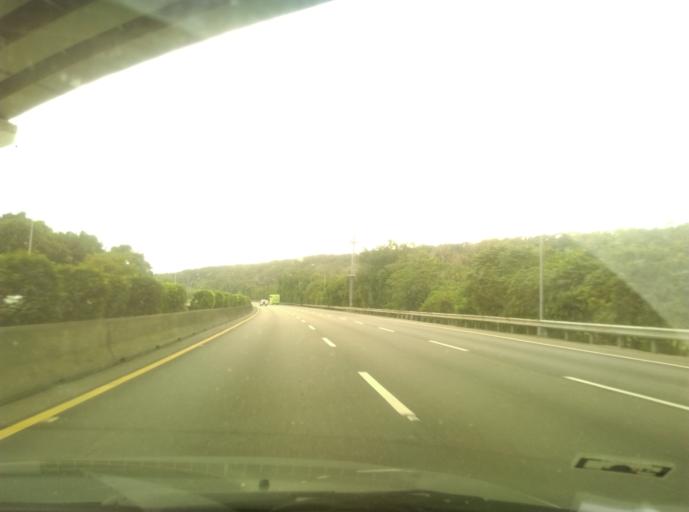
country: TW
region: Taiwan
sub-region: Taoyuan
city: Taoyuan
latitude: 24.9394
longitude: 121.3252
